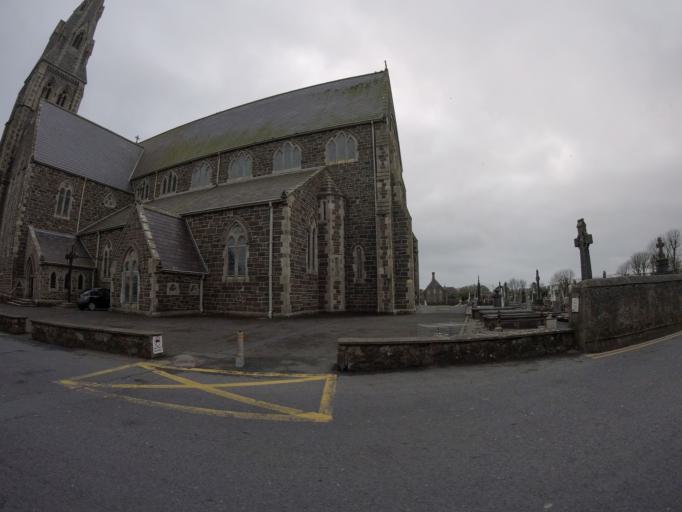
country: IE
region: Munster
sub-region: Waterford
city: Tra Mhor
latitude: 52.1635
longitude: -7.1568
